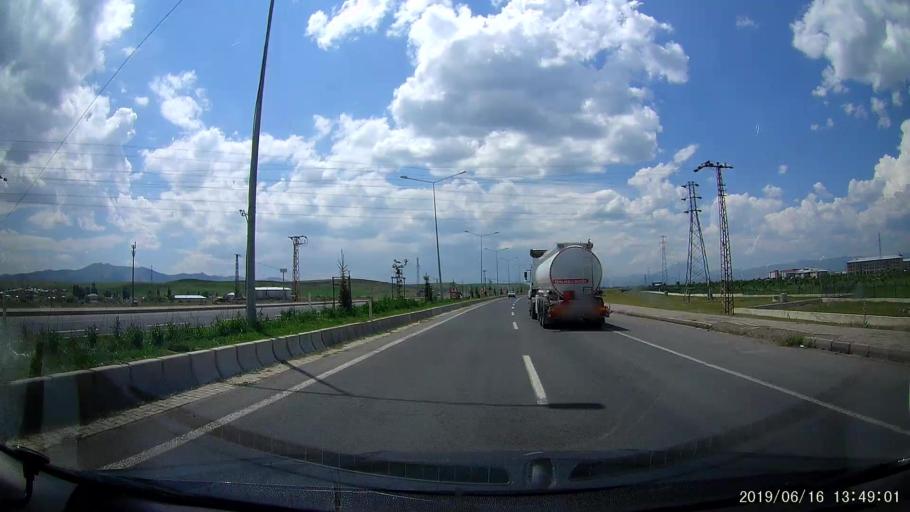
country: TR
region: Agri
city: Agri
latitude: 39.7151
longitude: 42.9968
